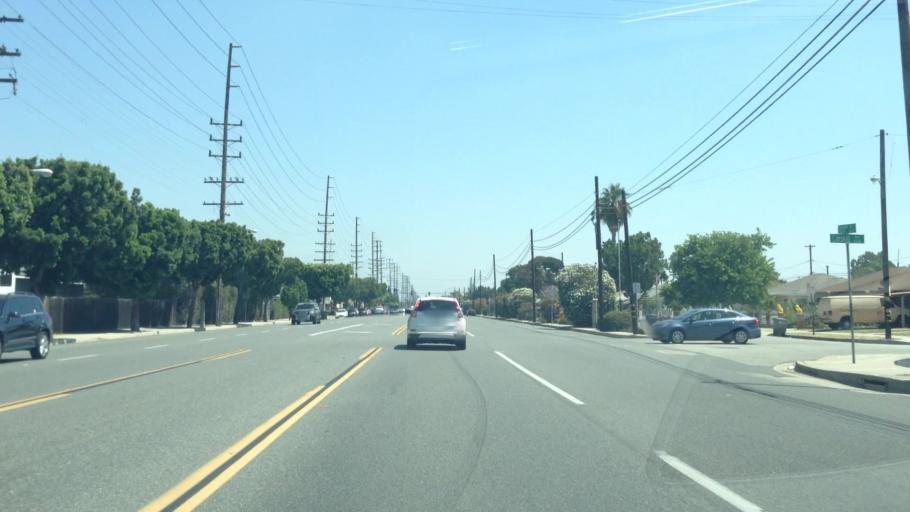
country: US
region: California
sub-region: Los Angeles County
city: Carson
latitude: 33.8242
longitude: -118.2718
